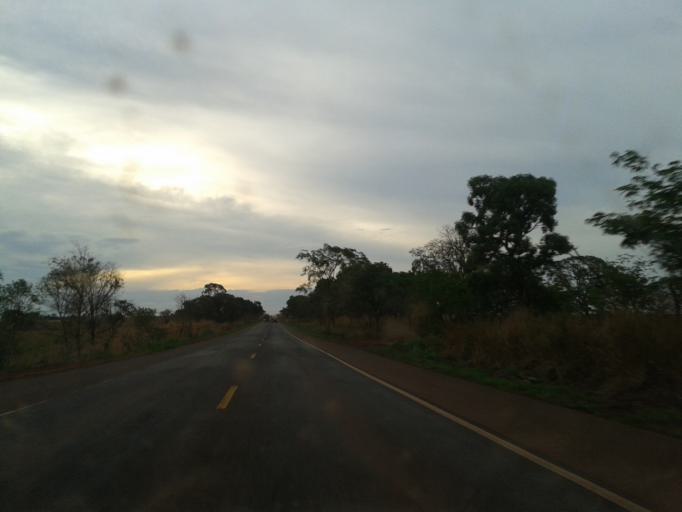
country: BR
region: Goias
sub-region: Santa Helena De Goias
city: Santa Helena de Goias
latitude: -17.9409
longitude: -50.5272
